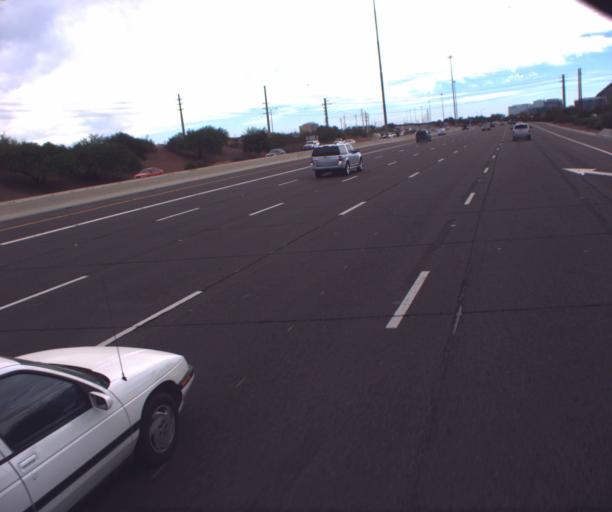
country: US
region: Arizona
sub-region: Maricopa County
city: Tempe Junction
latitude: 33.4372
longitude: -111.9597
